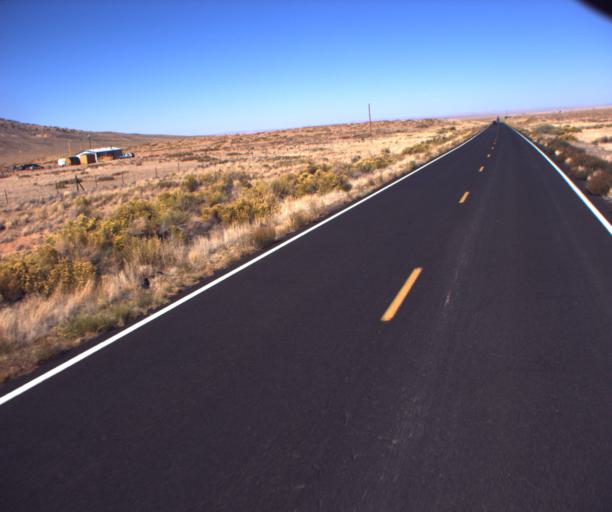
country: US
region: Arizona
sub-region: Navajo County
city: Dilkon
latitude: 35.4706
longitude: -110.4237
